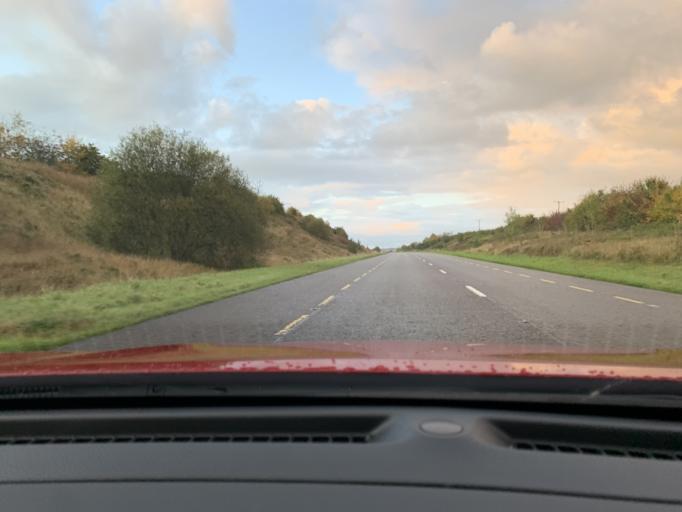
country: IE
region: Connaught
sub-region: Roscommon
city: Boyle
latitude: 54.0343
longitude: -8.3379
